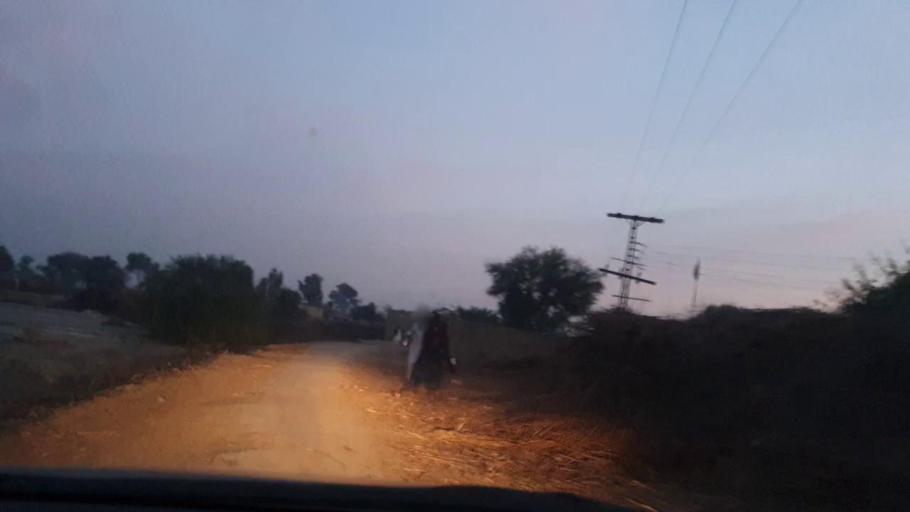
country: PK
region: Sindh
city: Sakrand
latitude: 26.1874
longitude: 68.3017
